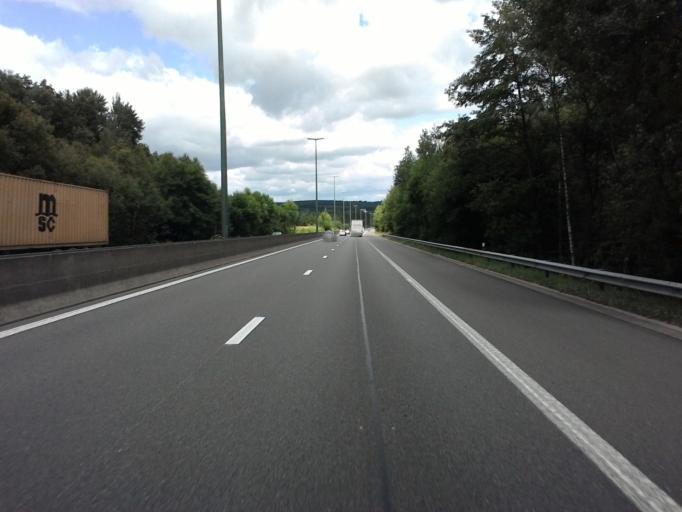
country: BE
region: Wallonia
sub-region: Province du Luxembourg
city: Leglise
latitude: 49.7871
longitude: 5.5319
